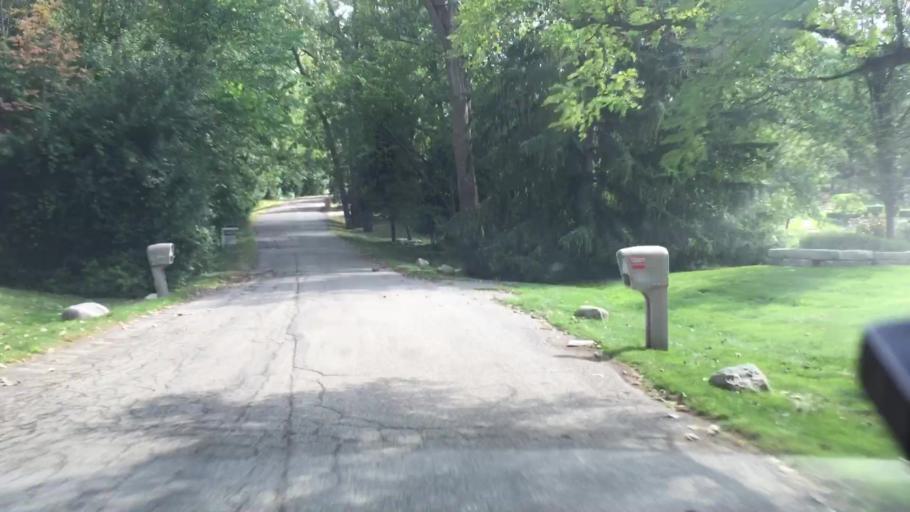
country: US
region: Michigan
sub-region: Oakland County
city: Sylvan Lake
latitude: 42.5728
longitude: -83.3153
